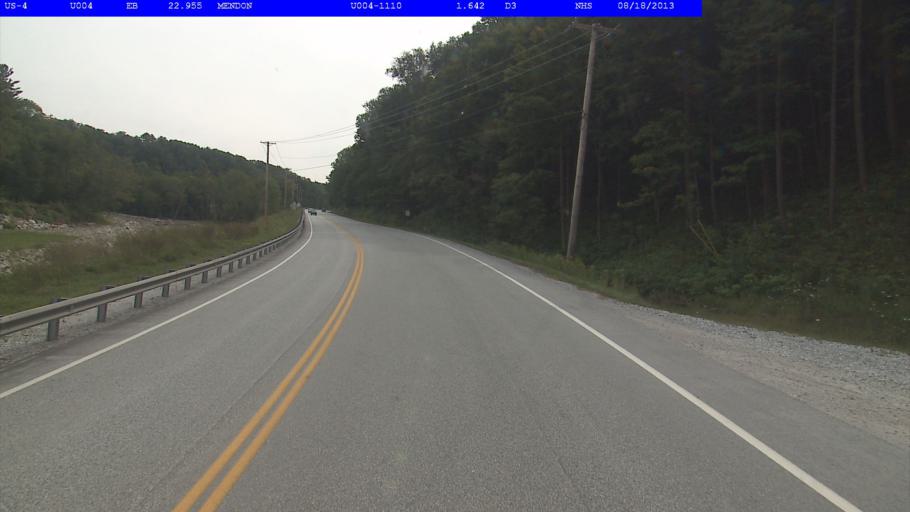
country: US
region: Vermont
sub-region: Rutland County
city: Rutland
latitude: 43.6514
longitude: -72.9204
